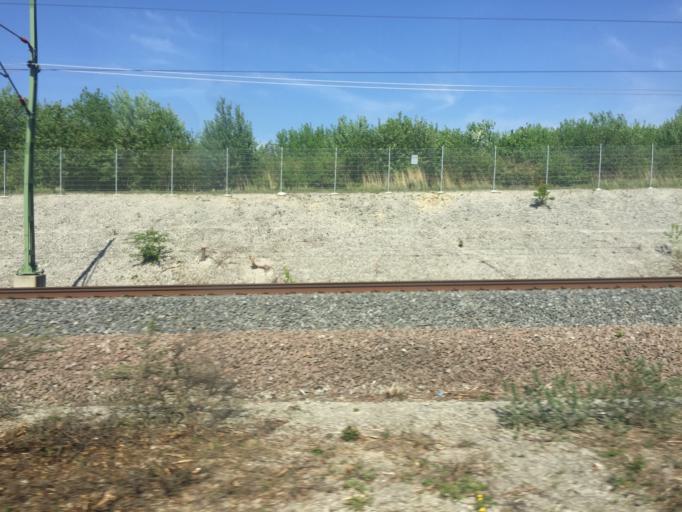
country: SE
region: Skane
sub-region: Malmo
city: Bunkeflostrand
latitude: 55.5587
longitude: 12.9488
